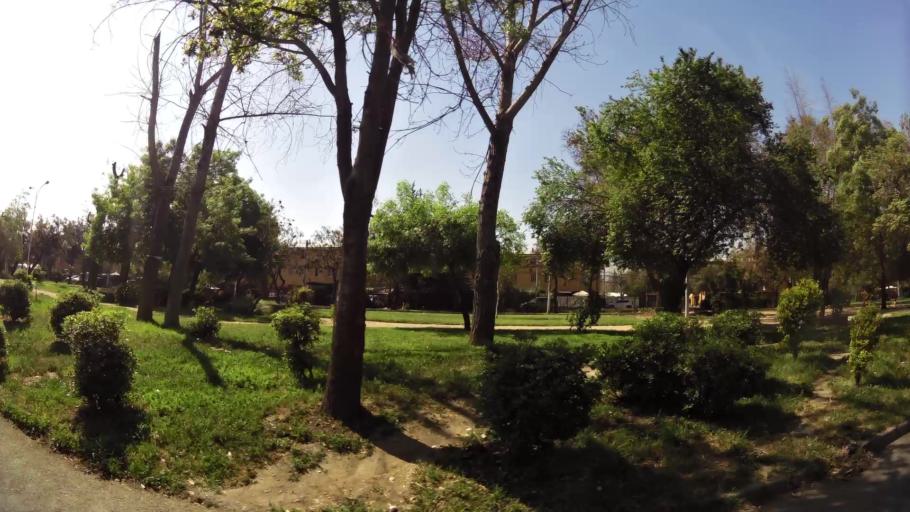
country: CL
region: Santiago Metropolitan
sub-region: Provincia de Santiago
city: Villa Presidente Frei, Nunoa, Santiago, Chile
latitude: -33.4879
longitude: -70.5845
